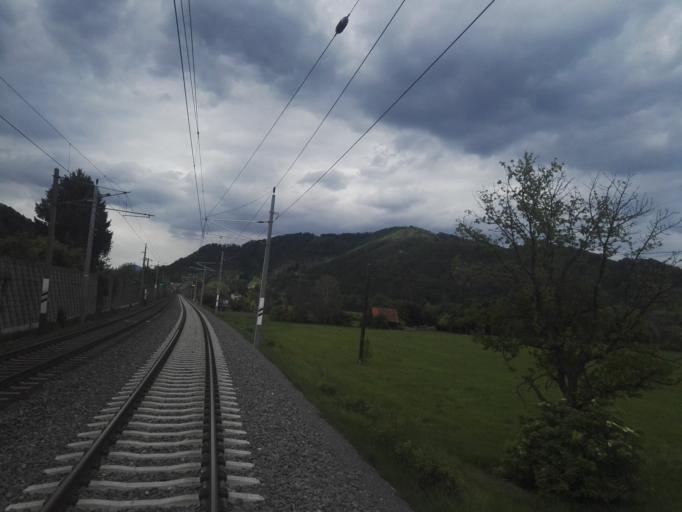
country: AT
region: Styria
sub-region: Politischer Bezirk Graz-Umgebung
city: Gratwein
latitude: 47.1395
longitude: 15.3235
